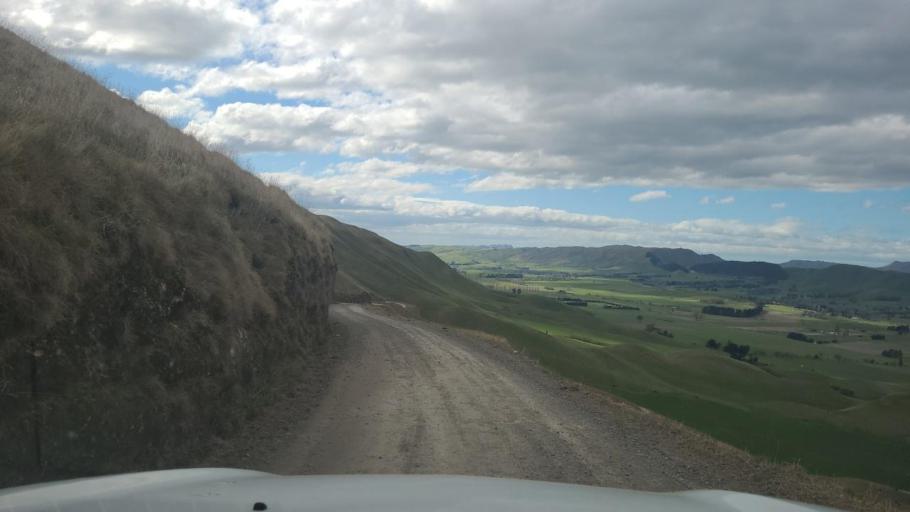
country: NZ
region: Hawke's Bay
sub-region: Hastings District
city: Hastings
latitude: -39.7551
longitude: 176.6814
